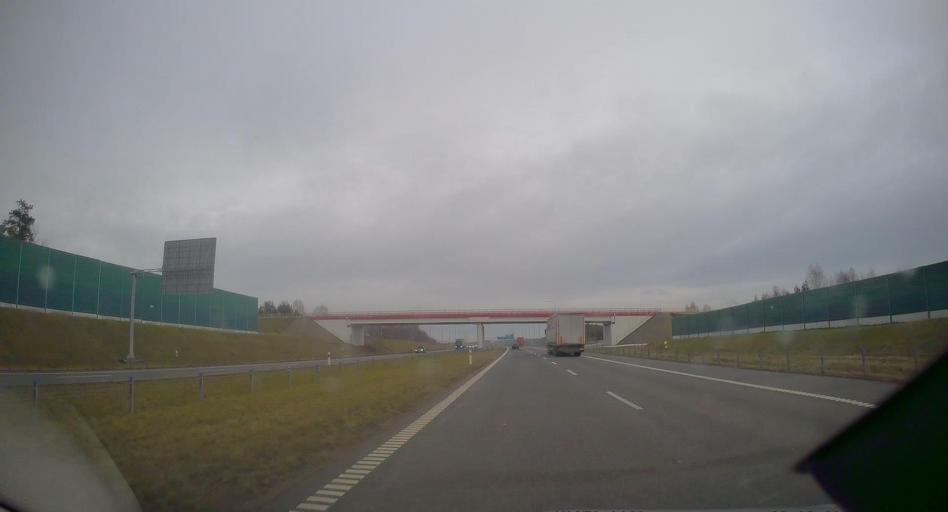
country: PL
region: Silesian Voivodeship
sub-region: Czestochowa
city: Czestochowa
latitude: 50.8750
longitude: 19.1290
